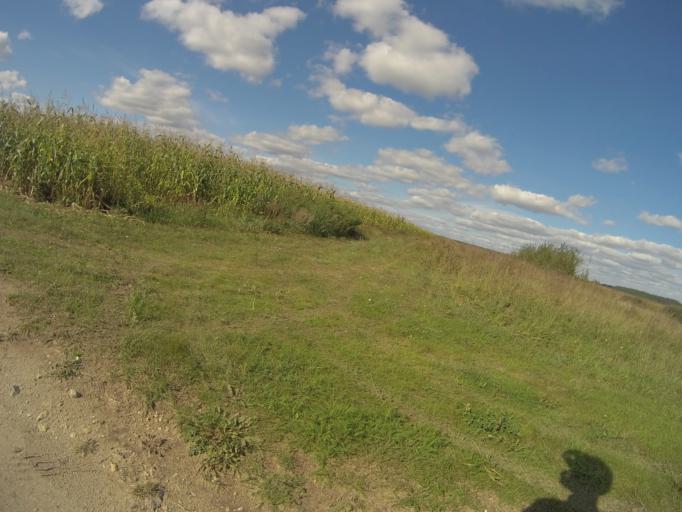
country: RU
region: Vladimir
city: Orgtrud
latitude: 56.3098
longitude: 40.6632
